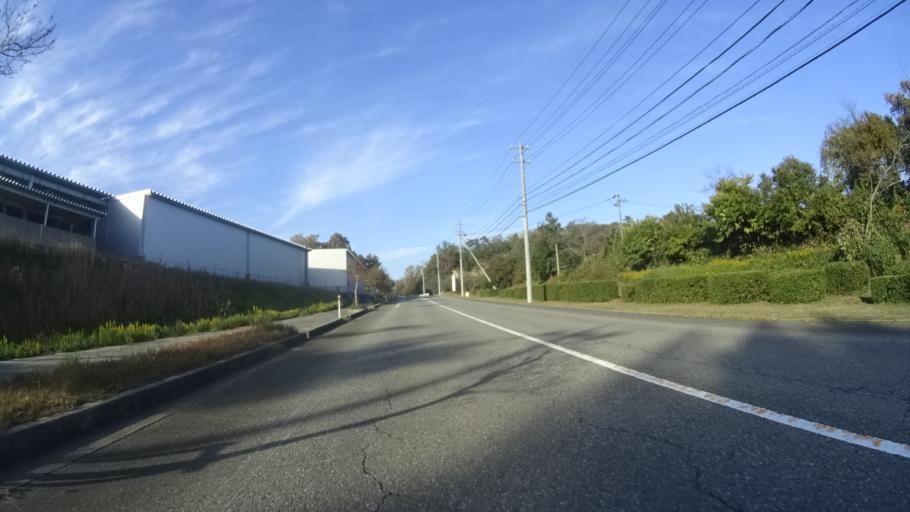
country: JP
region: Ishikawa
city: Hakui
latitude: 37.0361
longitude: 136.7786
